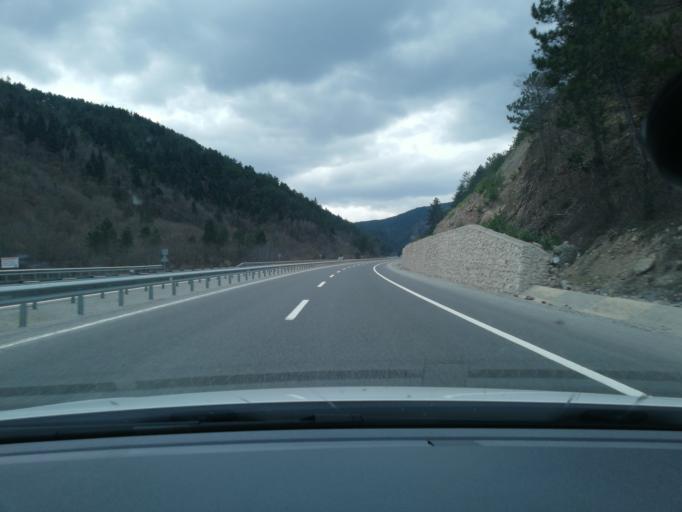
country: TR
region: Bolu
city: Yenicaga
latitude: 40.8501
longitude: 32.0677
